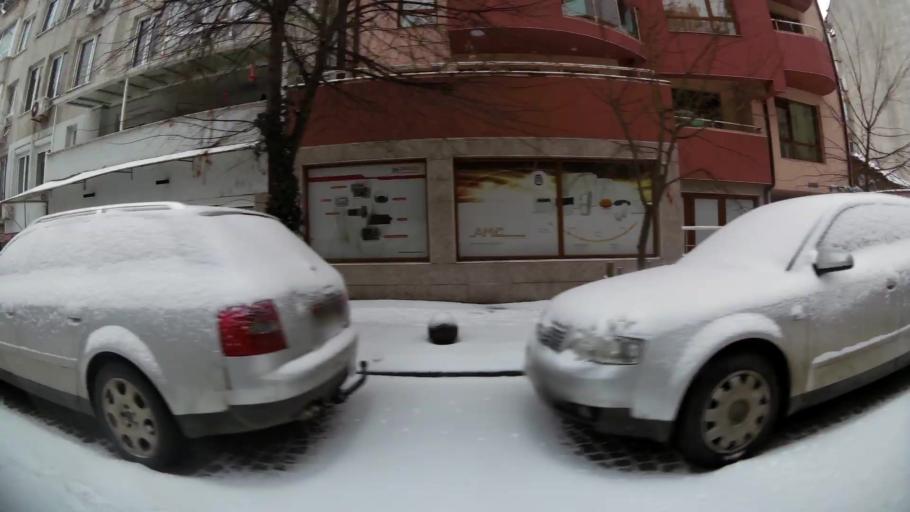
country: BG
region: Sofia-Capital
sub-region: Stolichna Obshtina
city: Sofia
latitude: 42.7039
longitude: 23.3092
